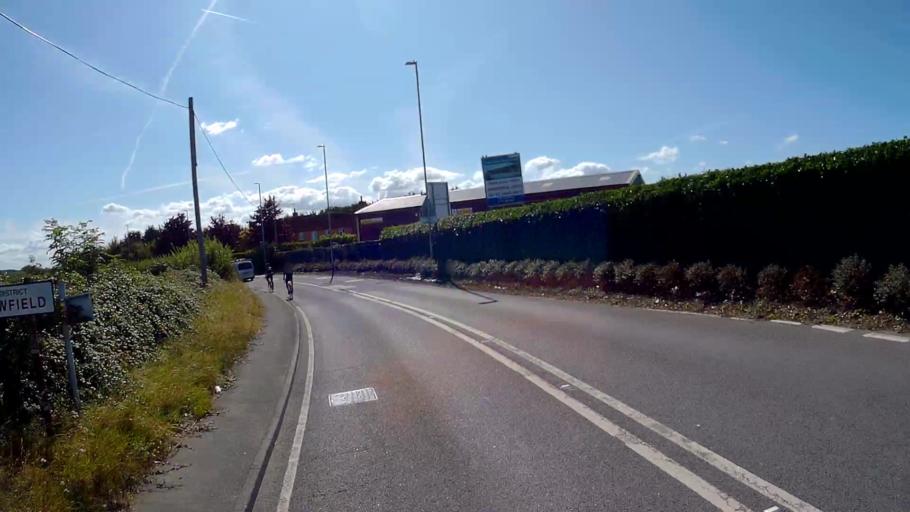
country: GB
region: England
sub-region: Wokingham
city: Swallowfield
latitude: 51.3854
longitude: -0.9732
